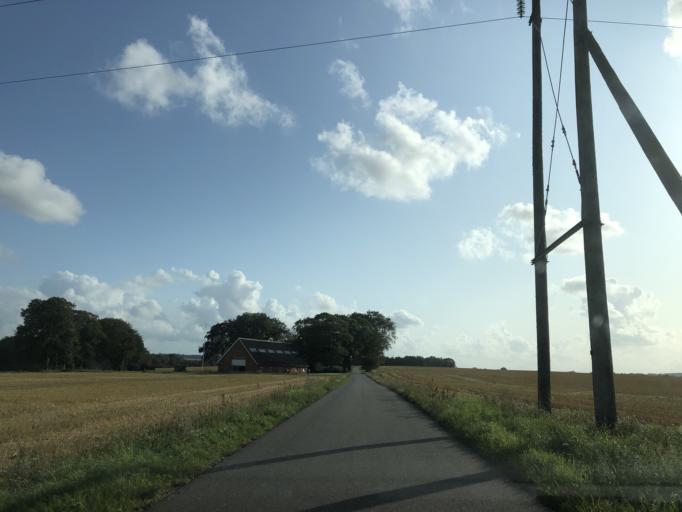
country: DK
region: Central Jutland
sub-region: Favrskov Kommune
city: Hammel
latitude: 56.2405
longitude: 9.7613
